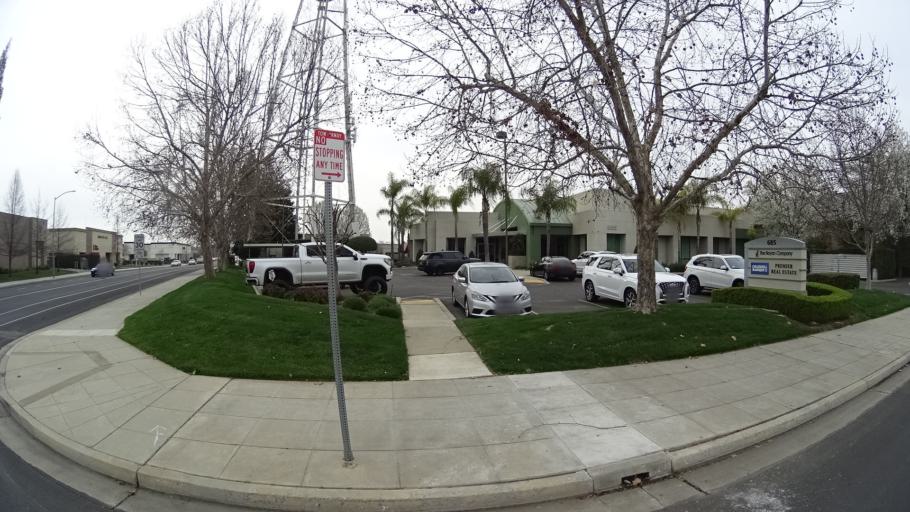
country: US
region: California
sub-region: Fresno County
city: Fresno
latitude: 36.8451
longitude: -119.8052
